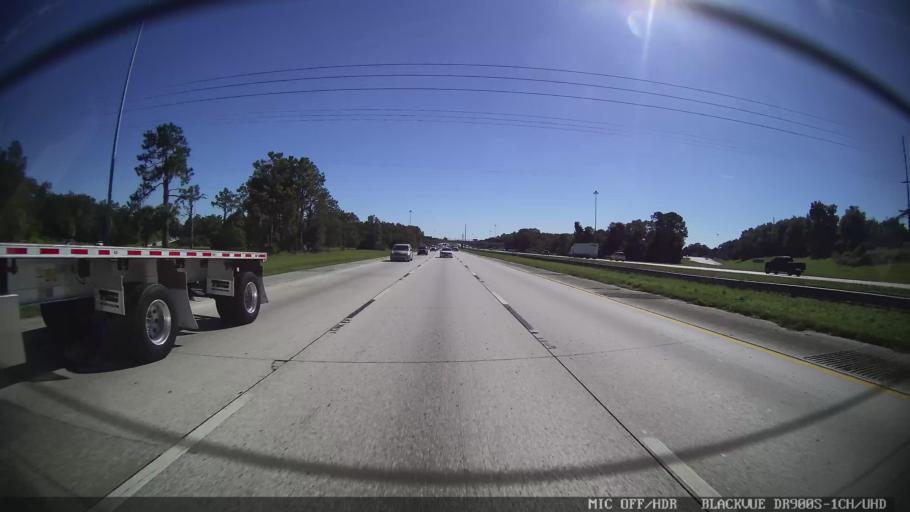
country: US
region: Florida
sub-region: Hillsborough County
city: Mango
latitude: 27.9909
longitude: -82.3251
